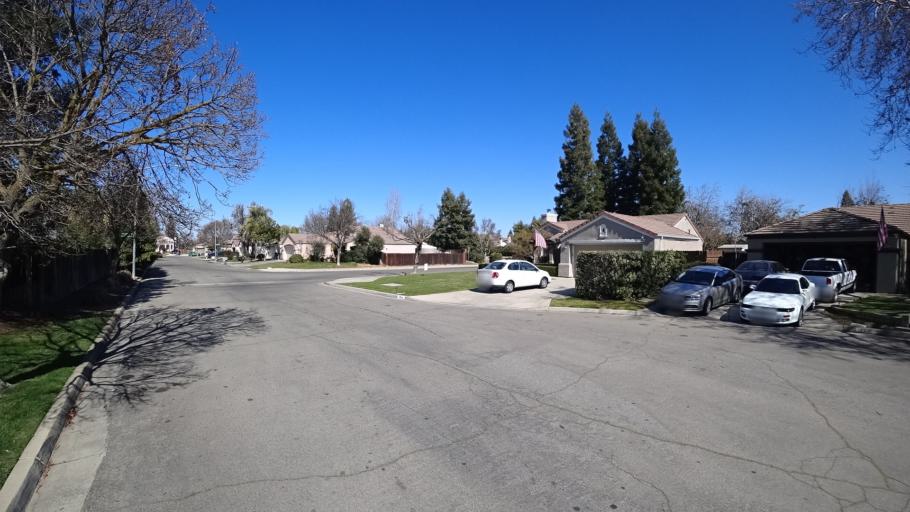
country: US
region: California
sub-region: Fresno County
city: Clovis
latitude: 36.8502
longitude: -119.7395
